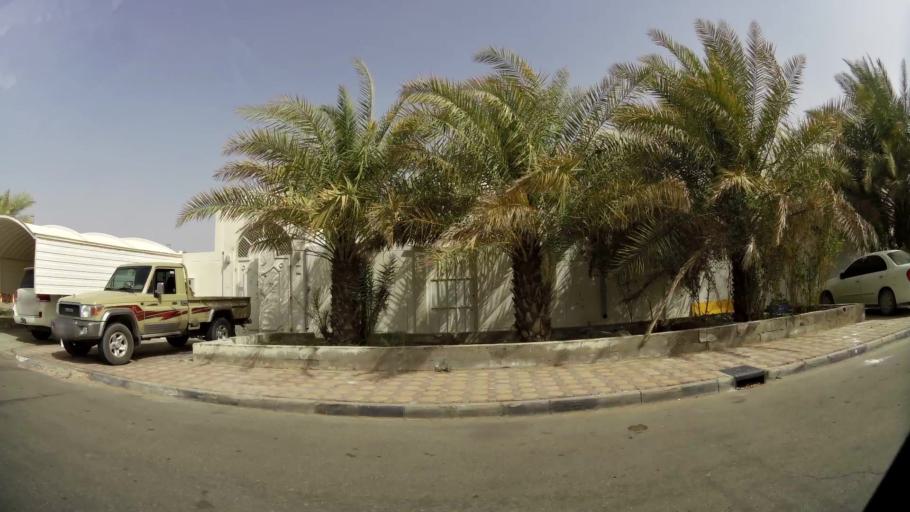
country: AE
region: Abu Dhabi
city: Al Ain
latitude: 24.1917
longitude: 55.6378
